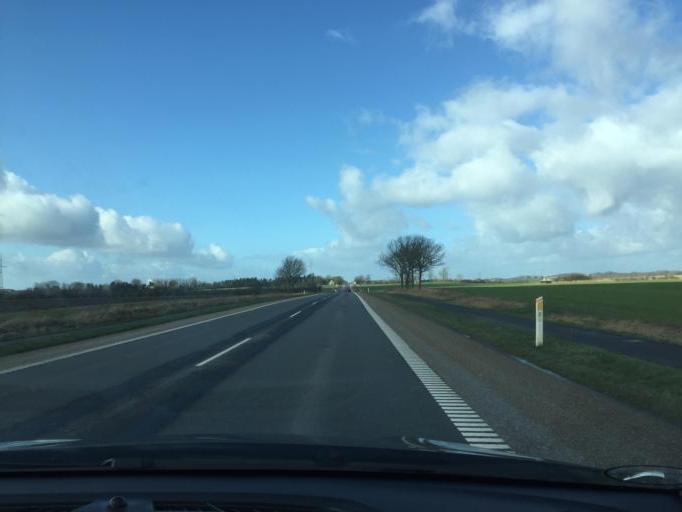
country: DK
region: South Denmark
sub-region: Middelfart Kommune
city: Norre Aby
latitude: 55.4844
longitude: 9.8262
